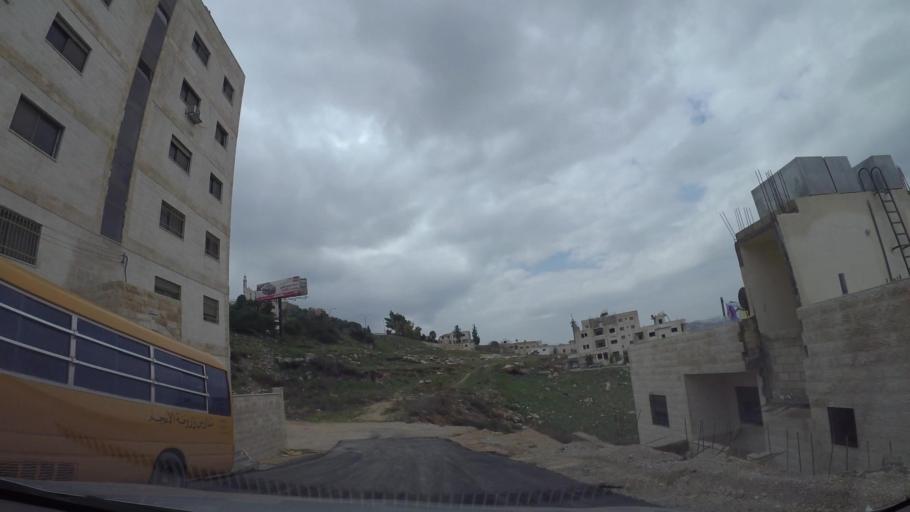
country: JO
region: Amman
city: Al Jubayhah
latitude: 32.0486
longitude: 35.8417
